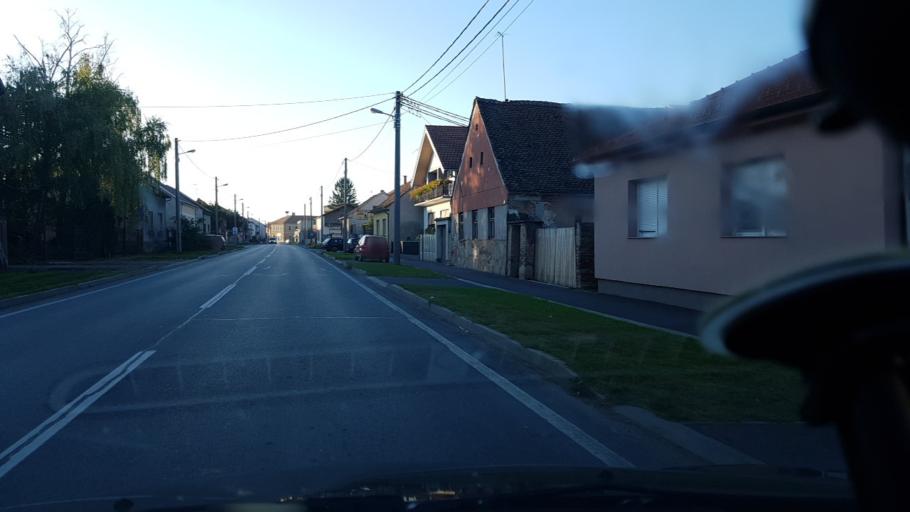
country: HR
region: Koprivnicko-Krizevacka
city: Virje
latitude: 46.0644
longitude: 16.9928
